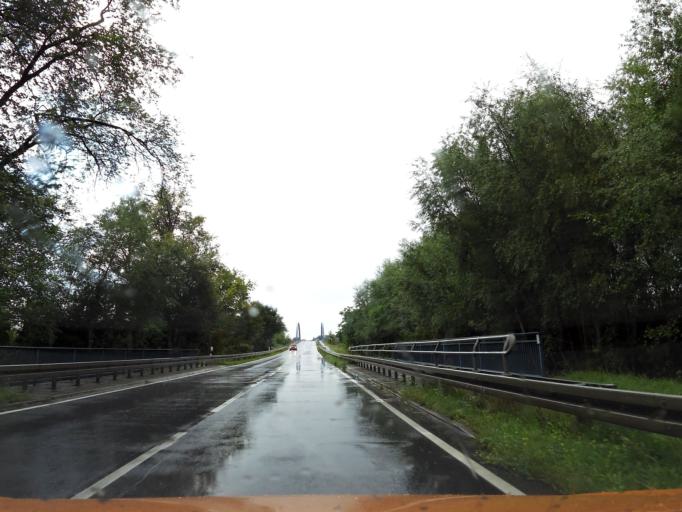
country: DE
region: Brandenburg
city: Wustermark
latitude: 52.4866
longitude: 12.9332
